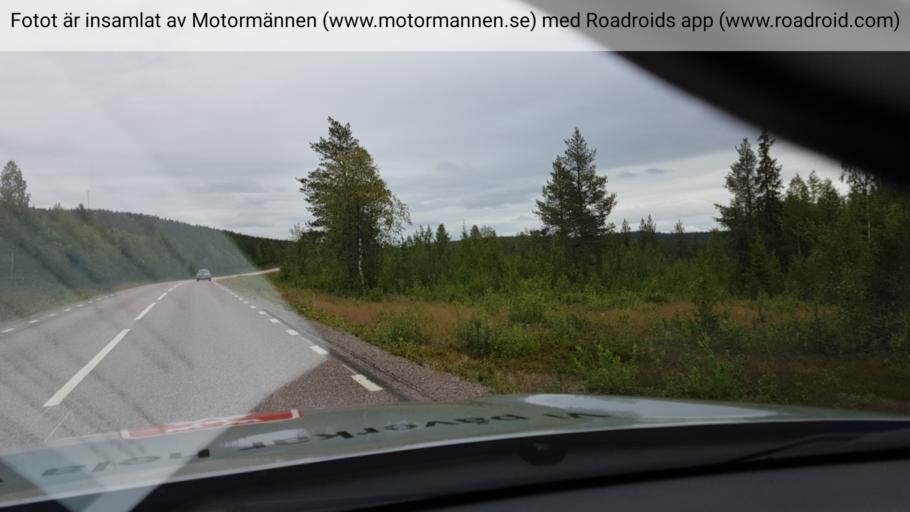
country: SE
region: Norrbotten
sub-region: Gallivare Kommun
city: Gaellivare
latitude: 67.0451
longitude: 21.6266
